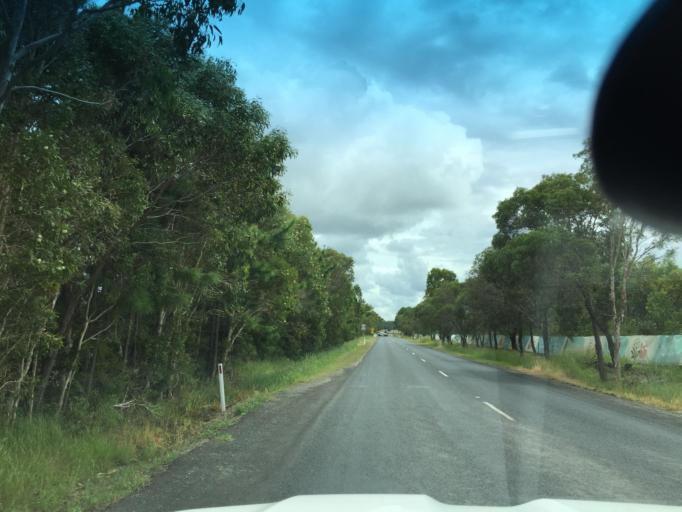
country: AU
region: Queensland
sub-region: Moreton Bay
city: Morayfield
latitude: -27.1127
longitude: 152.9801
